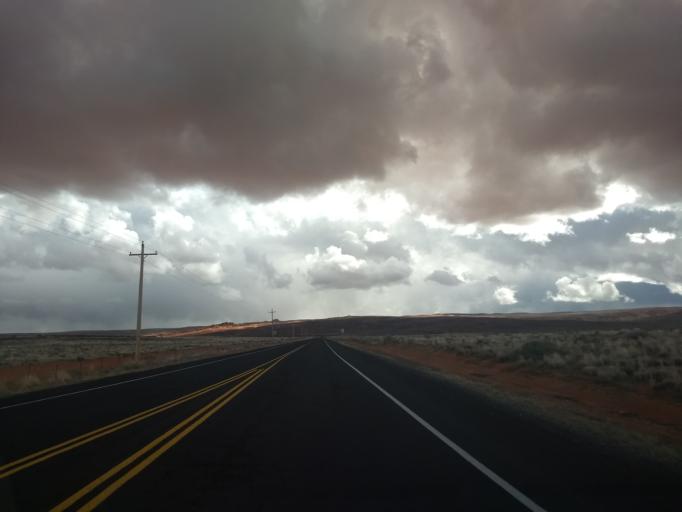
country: US
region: Utah
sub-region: Washington County
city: Hurricane
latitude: 37.1319
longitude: -113.3927
